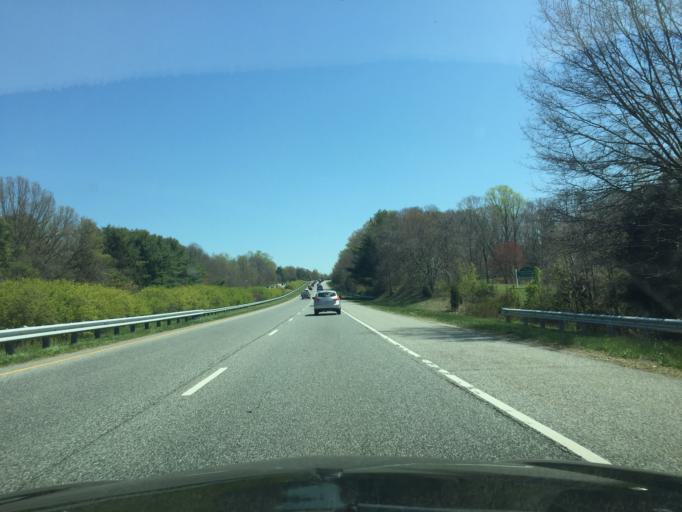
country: US
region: Maryland
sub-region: Harford County
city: Bel Air South
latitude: 39.5060
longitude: -76.3383
